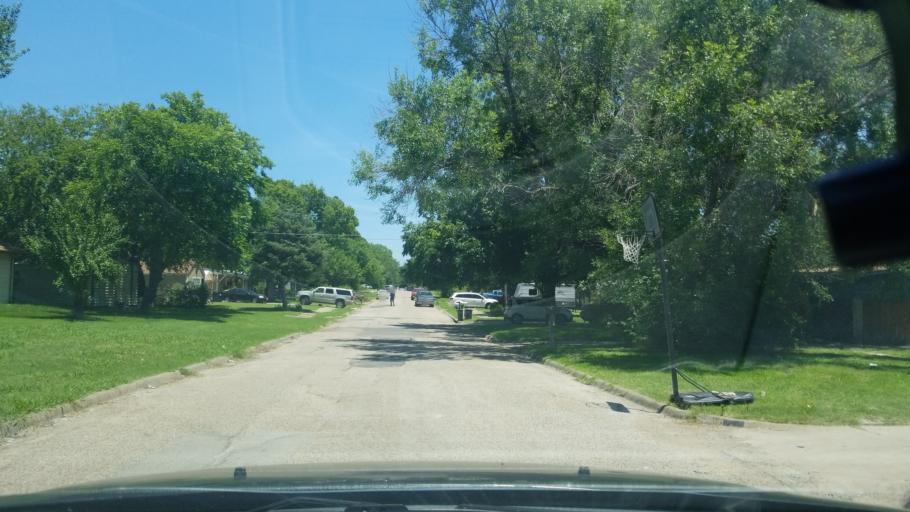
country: US
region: Texas
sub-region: Dallas County
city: Mesquite
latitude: 32.7798
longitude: -96.6054
